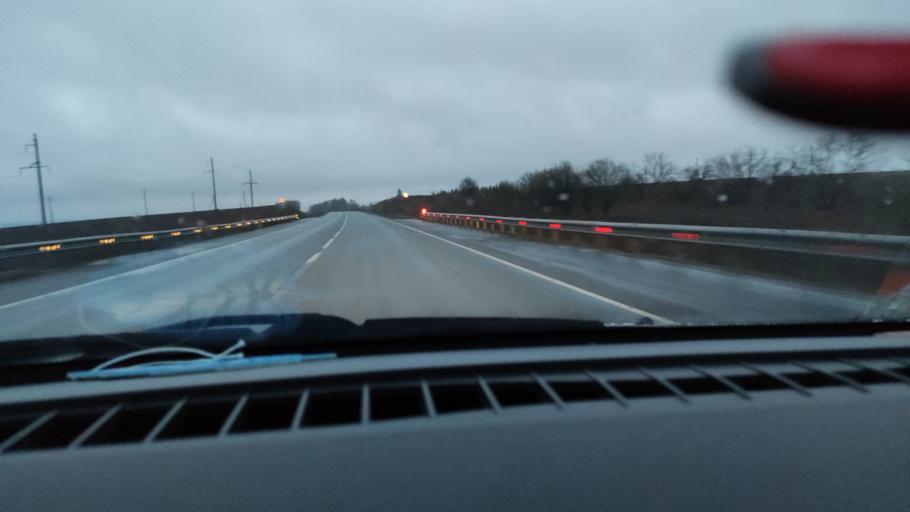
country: RU
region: Udmurtiya
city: Alnashi
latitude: 56.2247
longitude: 52.4134
